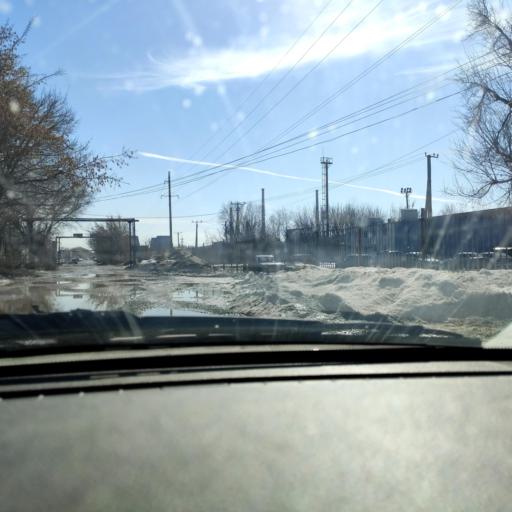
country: RU
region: Samara
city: Tol'yatti
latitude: 53.5893
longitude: 49.2583
